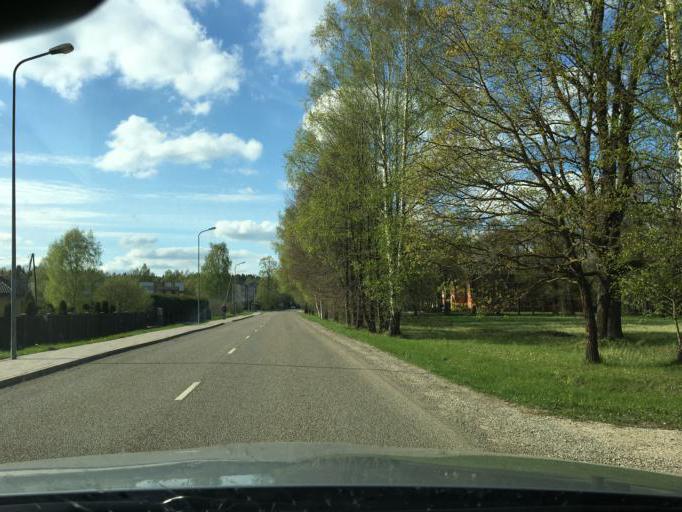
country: LV
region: Ozolnieku
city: Ozolnieki
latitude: 56.6813
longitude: 23.8377
